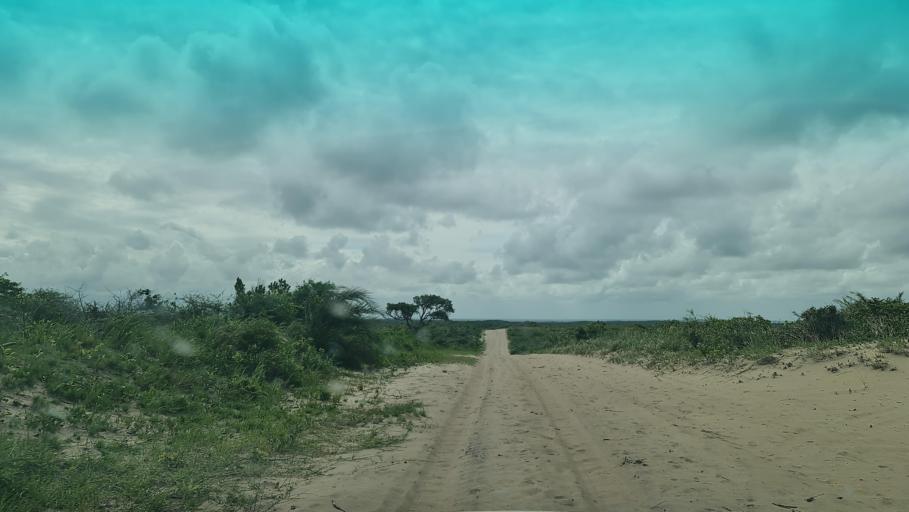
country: MZ
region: Maputo
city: Manhica
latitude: -25.4433
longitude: 32.9456
